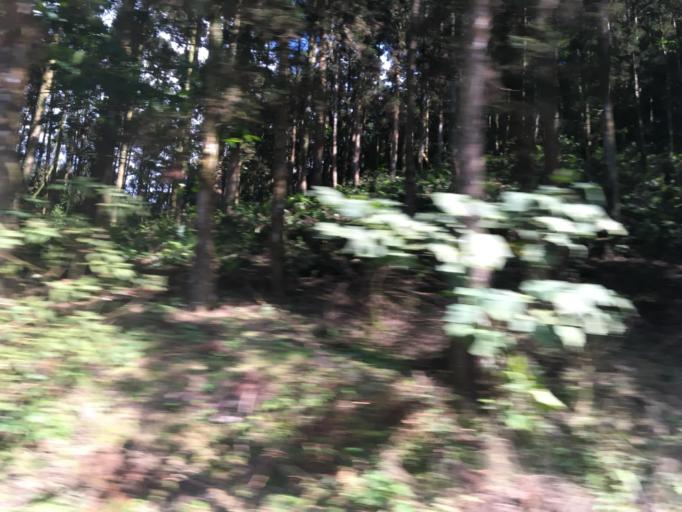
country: TW
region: Taiwan
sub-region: Yilan
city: Yilan
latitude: 24.7534
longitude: 121.6239
